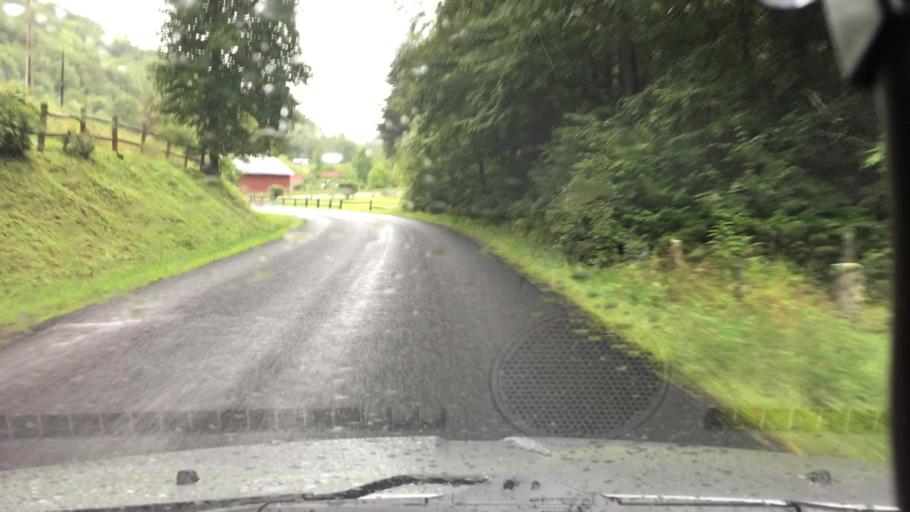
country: US
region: North Carolina
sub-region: Madison County
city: Mars Hill
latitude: 35.9131
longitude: -82.4986
